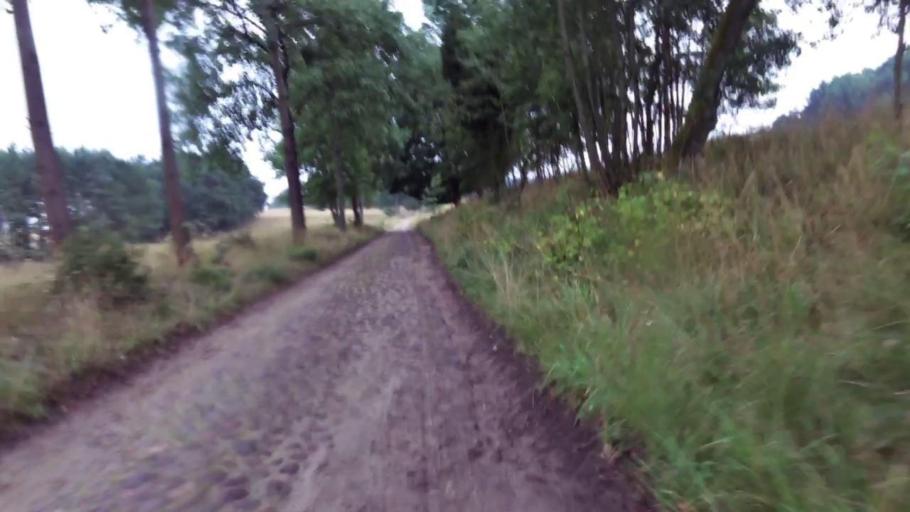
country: PL
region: West Pomeranian Voivodeship
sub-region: Powiat szczecinecki
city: Lubowo
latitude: 53.6138
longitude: 16.3359
